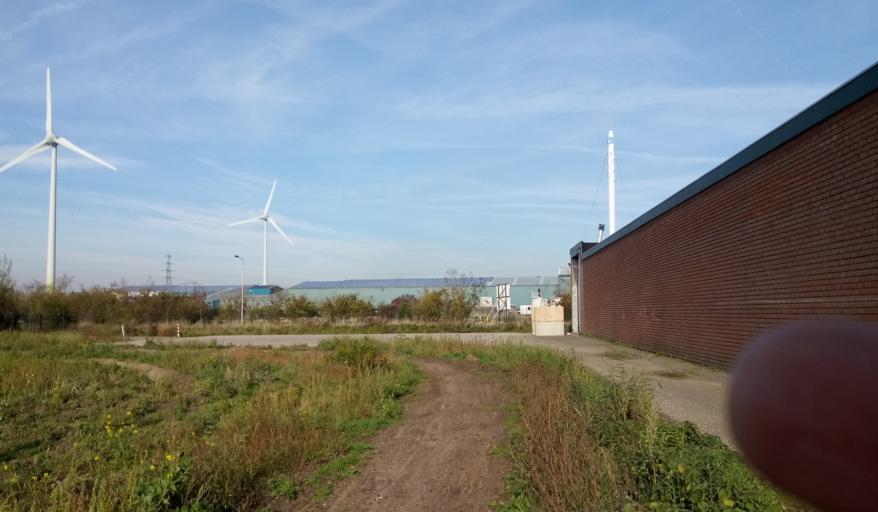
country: NL
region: Gelderland
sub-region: Gemeente Zutphen
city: Zutphen
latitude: 52.1582
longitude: 6.1942
